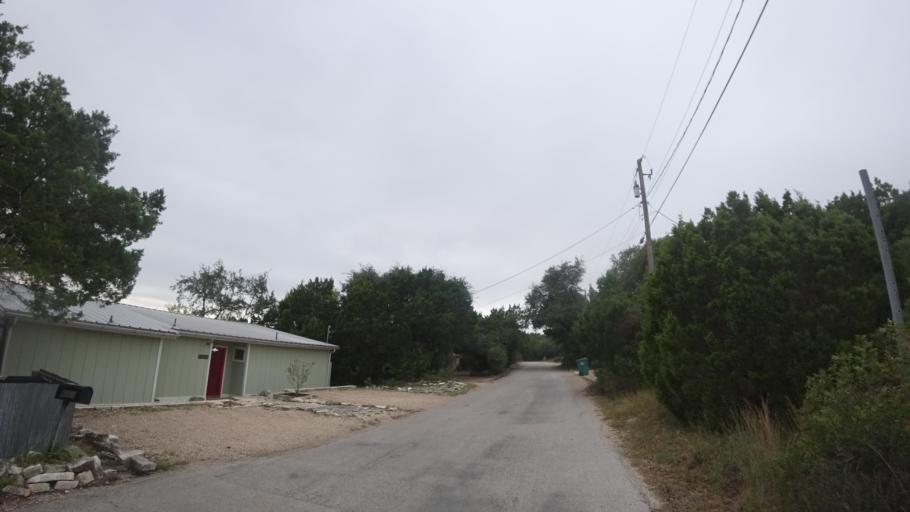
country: US
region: Texas
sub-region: Travis County
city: Hudson Bend
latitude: 30.3962
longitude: -97.9188
